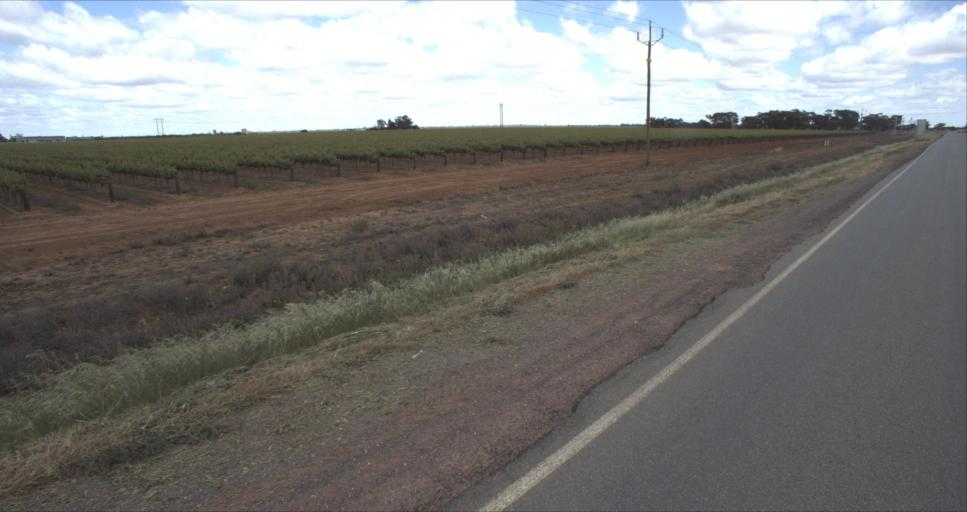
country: AU
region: New South Wales
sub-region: Murrumbidgee Shire
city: Darlington Point
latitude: -34.4970
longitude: 146.1872
